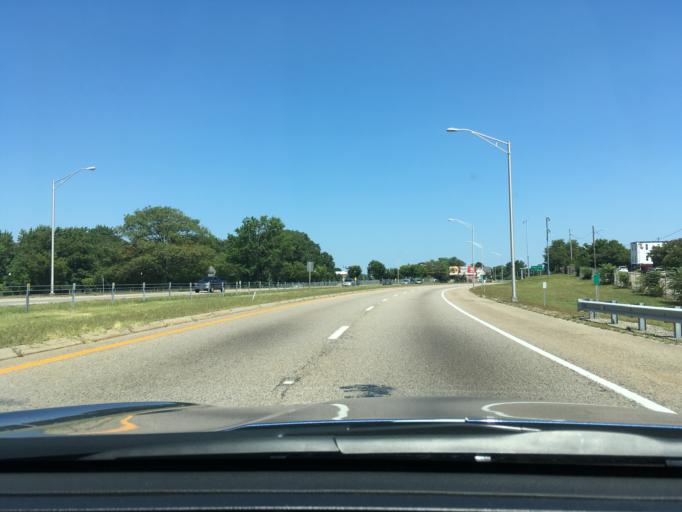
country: US
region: Rhode Island
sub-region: Providence County
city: Cranston
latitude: 41.7958
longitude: -71.4412
